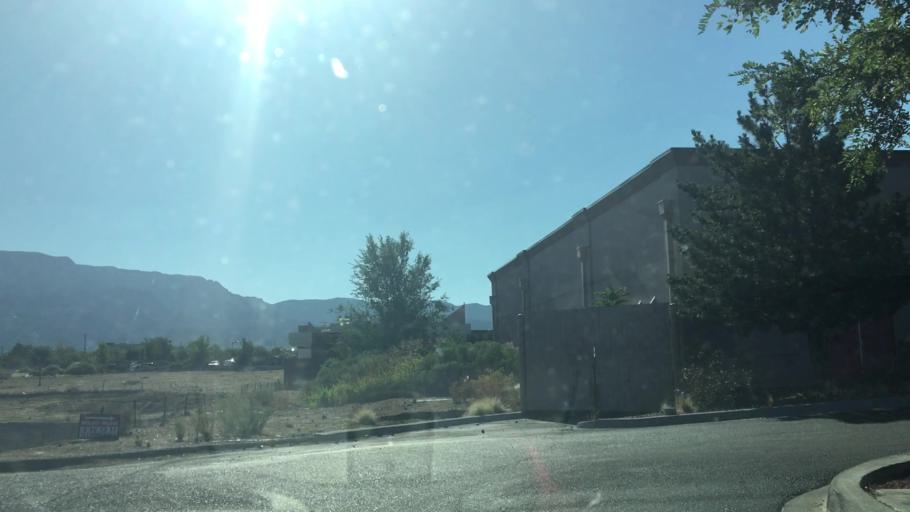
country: US
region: New Mexico
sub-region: Bernalillo County
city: North Valley
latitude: 35.1752
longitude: -106.5677
